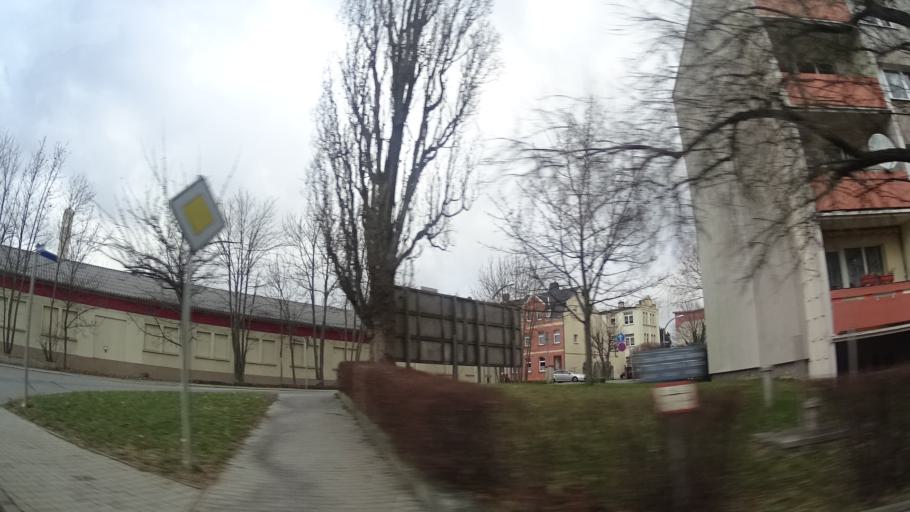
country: DE
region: Thuringia
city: Zeulenroda
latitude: 50.6448
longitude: 11.9844
